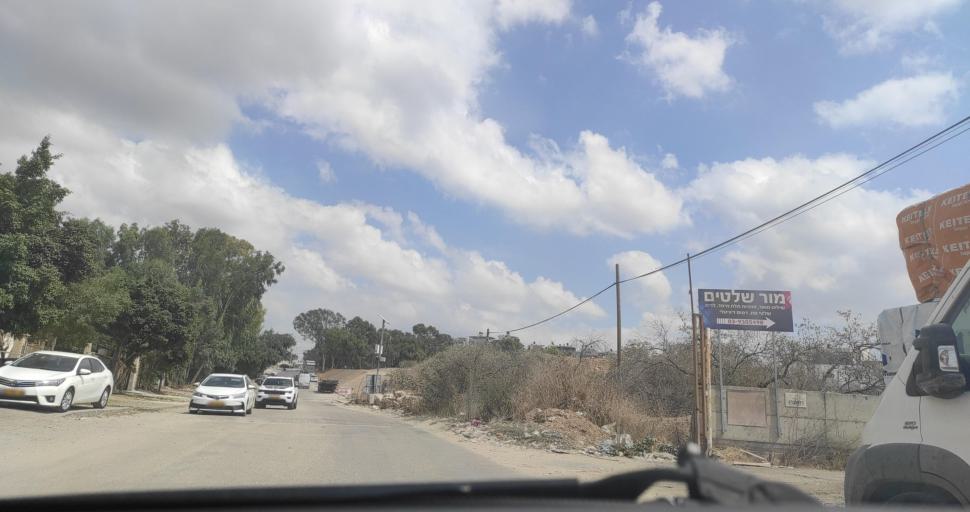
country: IL
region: Central District
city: Kafr Qasim
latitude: 32.1163
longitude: 34.9607
